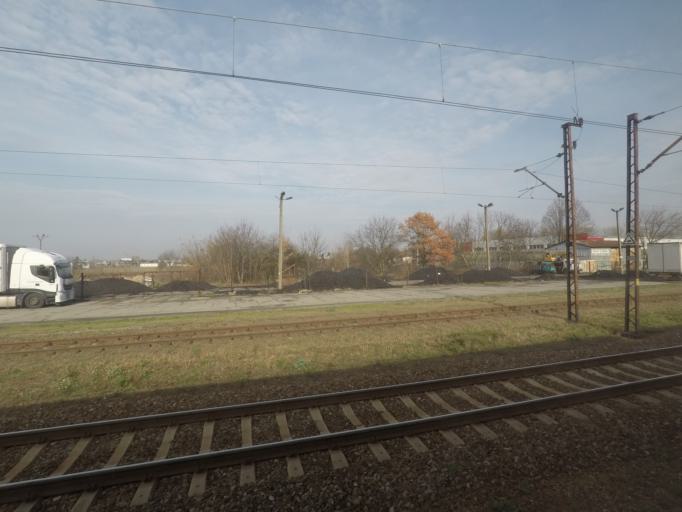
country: PL
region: Subcarpathian Voivodeship
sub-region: Powiat lancucki
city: Lancut
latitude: 50.0818
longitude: 22.2302
